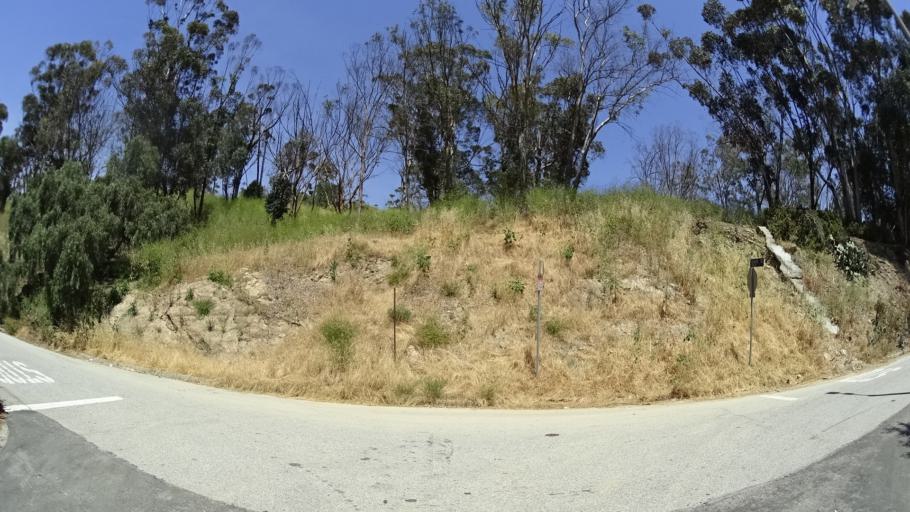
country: US
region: California
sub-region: Los Angeles County
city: Echo Park
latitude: 34.0785
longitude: -118.2341
